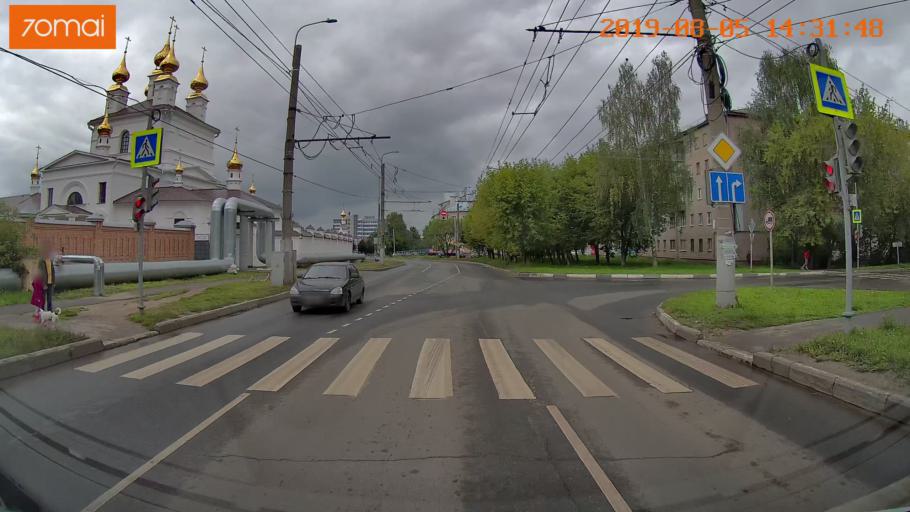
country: RU
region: Ivanovo
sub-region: Gorod Ivanovo
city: Ivanovo
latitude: 56.9887
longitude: 40.9972
